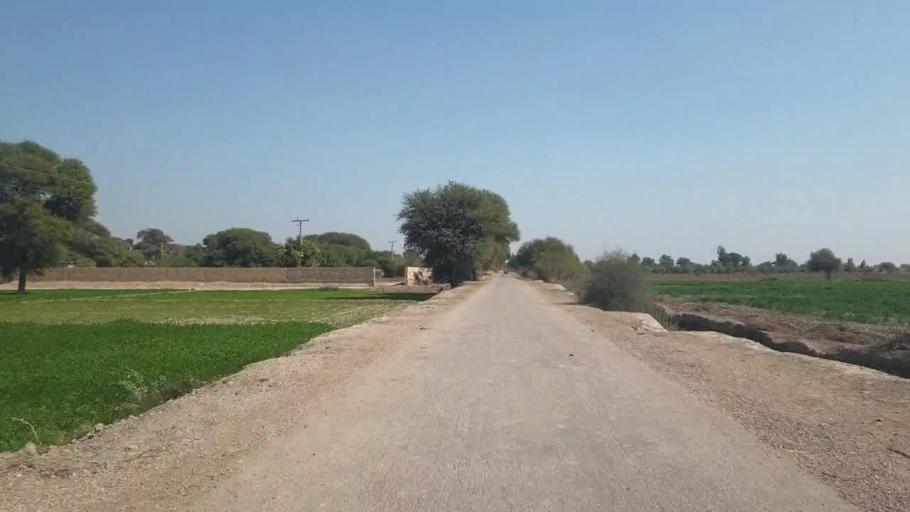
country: PK
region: Sindh
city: Chambar
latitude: 25.2887
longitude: 68.6794
